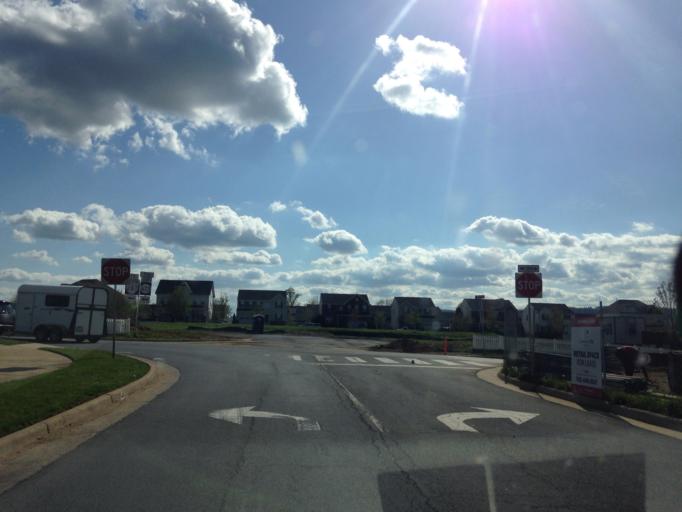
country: US
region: Virginia
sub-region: Loudoun County
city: Lovettsville
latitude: 39.2750
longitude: -77.6397
